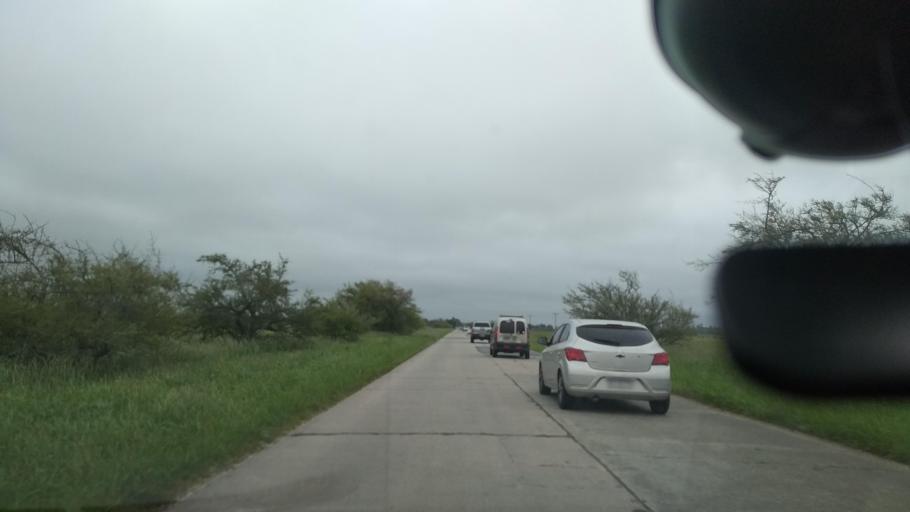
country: AR
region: Buenos Aires
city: Veronica
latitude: -35.5442
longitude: -57.3139
